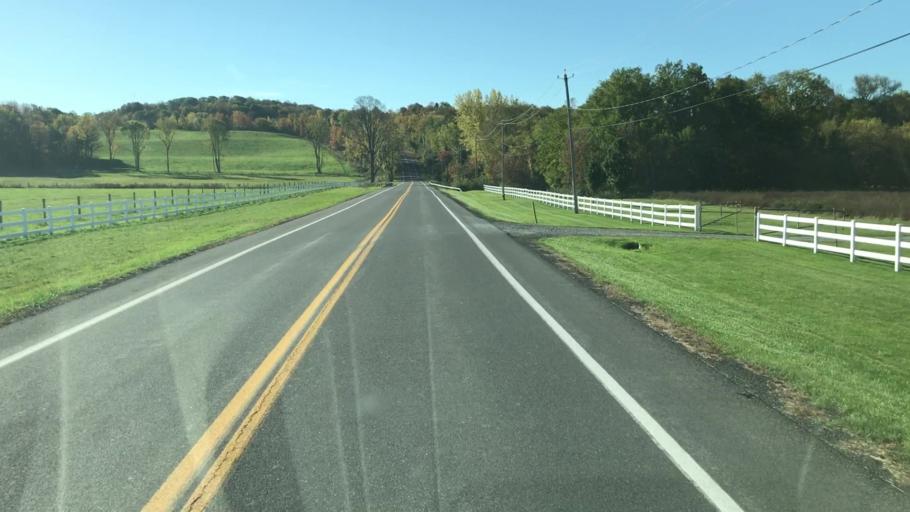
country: US
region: New York
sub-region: Onondaga County
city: Fayetteville
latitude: 42.9916
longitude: -76.0451
